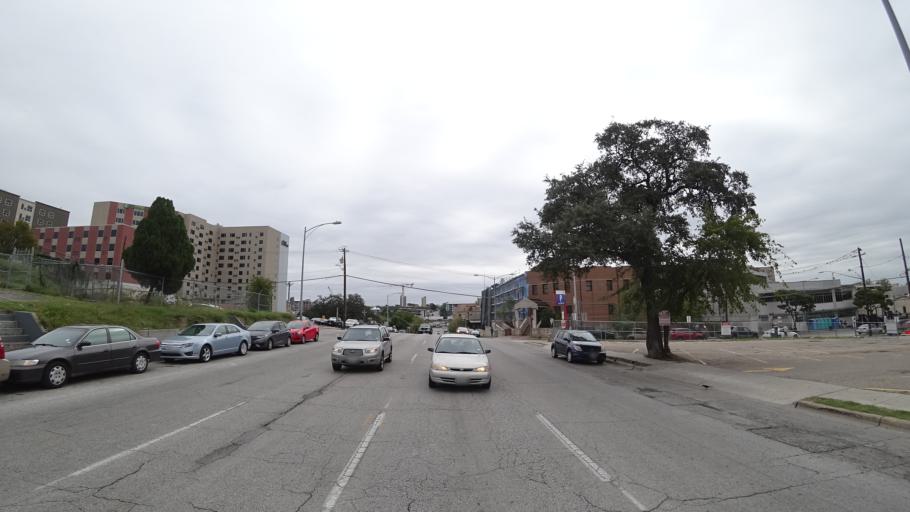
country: US
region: Texas
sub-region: Travis County
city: Austin
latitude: 30.2688
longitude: -97.7379
